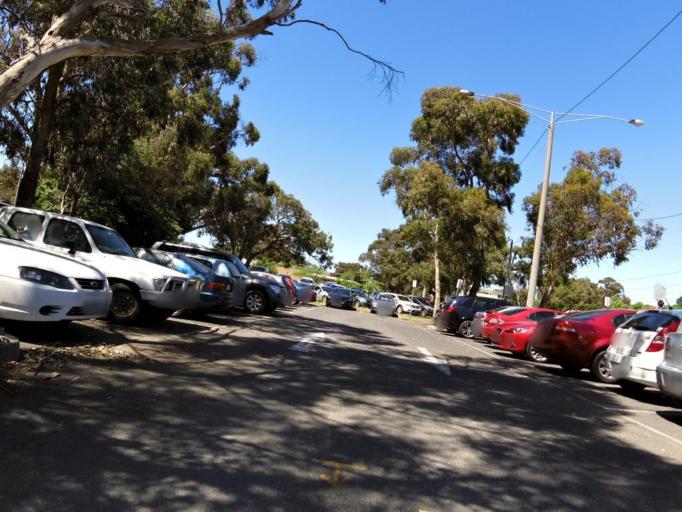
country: AU
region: Victoria
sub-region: Knox
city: Ferntree Gully
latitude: -37.8815
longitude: 145.2956
